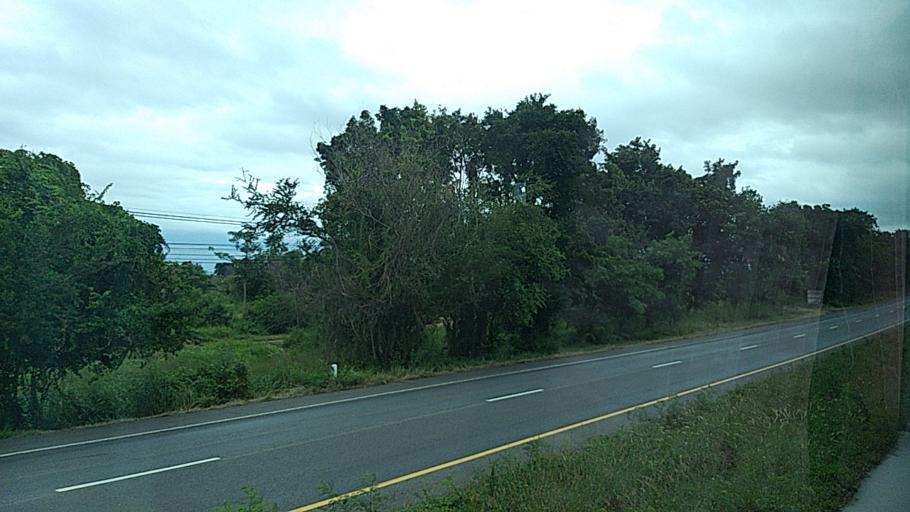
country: TH
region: Khon Kaen
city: Non Sila
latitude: 15.9067
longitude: 102.6555
